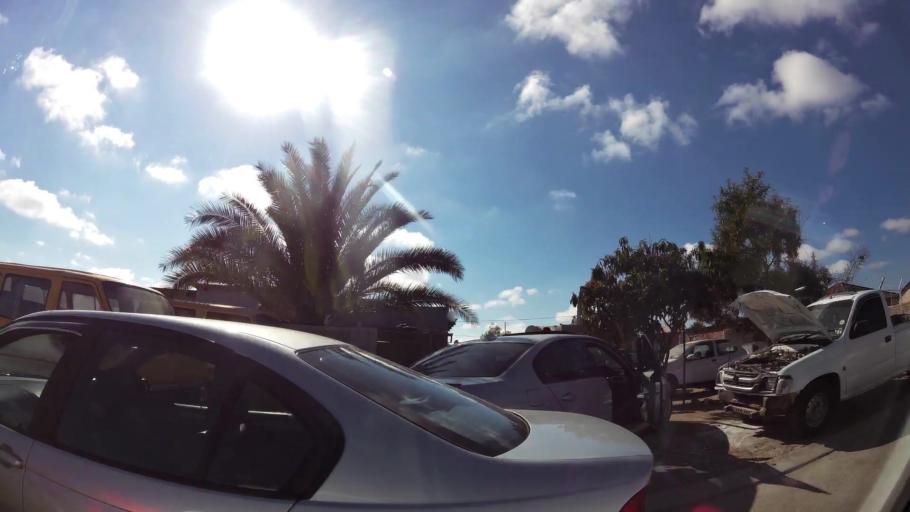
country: ZA
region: Limpopo
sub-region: Capricorn District Municipality
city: Polokwane
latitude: -23.8572
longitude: 29.3634
